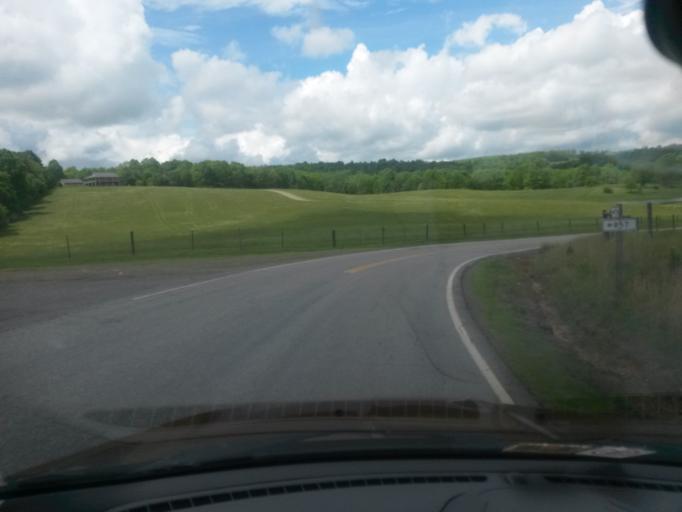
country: US
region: Virginia
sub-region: Patrick County
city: Stuart
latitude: 36.7494
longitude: -80.3933
